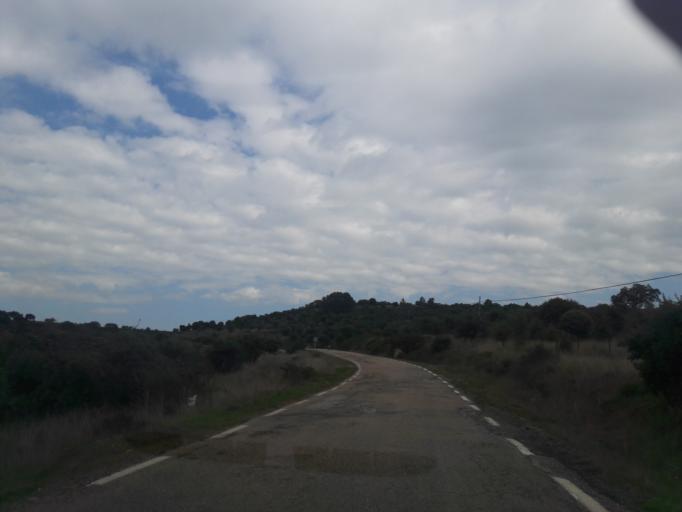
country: ES
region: Castille and Leon
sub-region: Provincia de Salamanca
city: Serradilla del Arroyo
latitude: 40.5253
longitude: -6.3821
